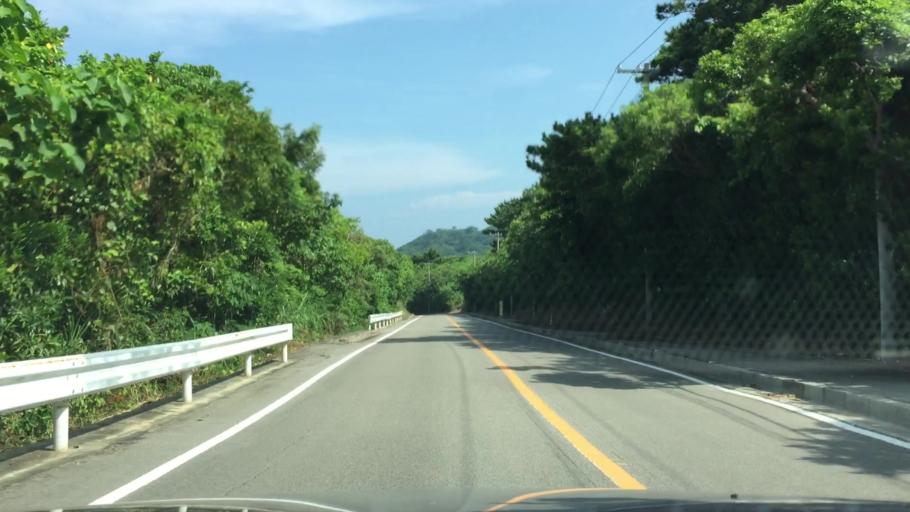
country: JP
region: Okinawa
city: Ishigaki
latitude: 24.5113
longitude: 124.2673
